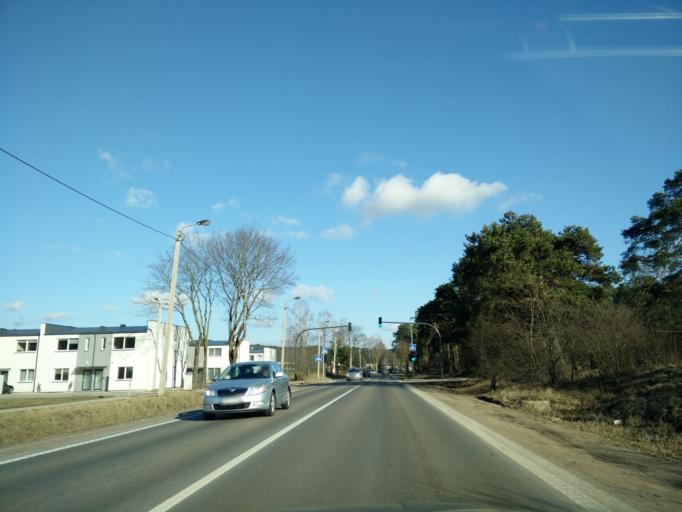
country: LT
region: Kauno apskritis
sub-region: Kauno rajonas
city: Akademija (Kaunas)
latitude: 54.9208
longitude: 23.8066
